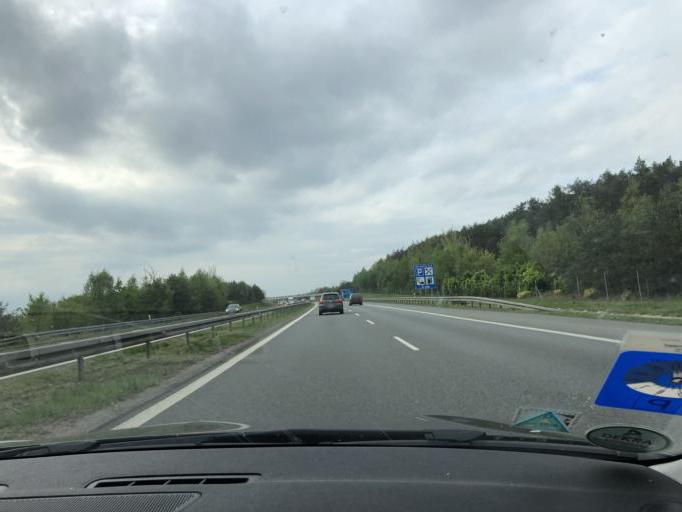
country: PL
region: Opole Voivodeship
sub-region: Powiat opolski
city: Dabrowa
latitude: 50.6494
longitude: 17.7243
